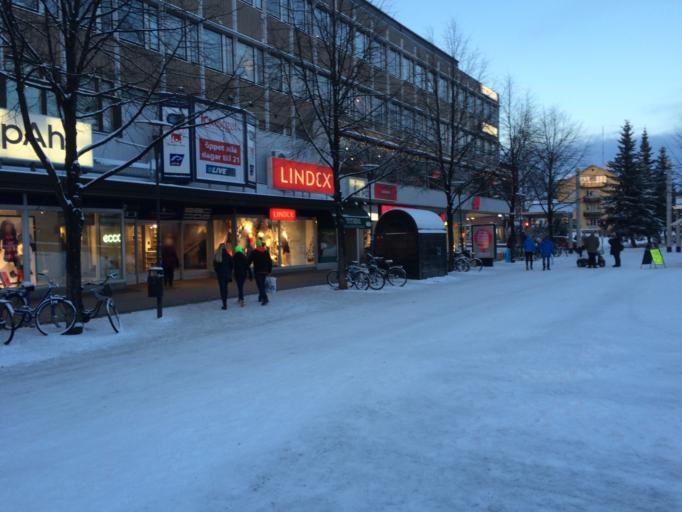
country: SE
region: Vaesterbotten
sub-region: Skelleftea Kommun
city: Skelleftea
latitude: 64.7511
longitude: 20.9533
